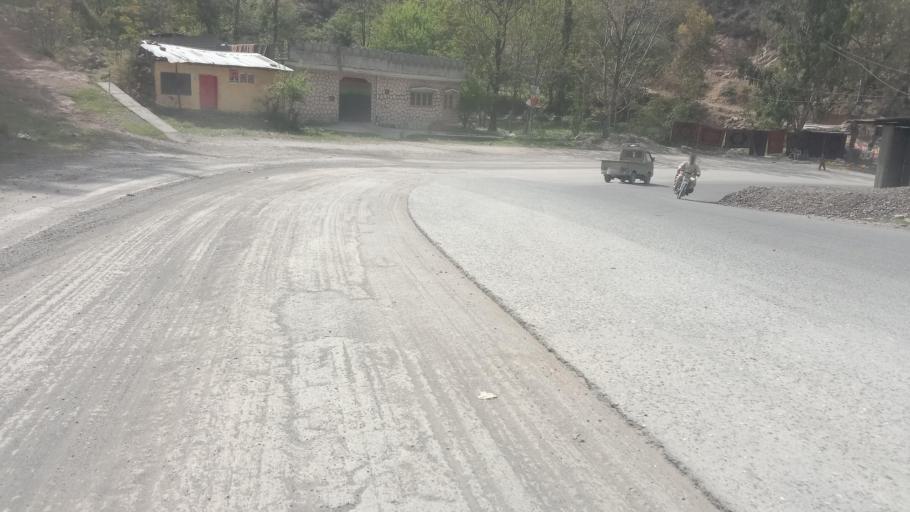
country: PK
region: Khyber Pakhtunkhwa
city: Abbottabad
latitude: 34.1215
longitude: 73.1842
